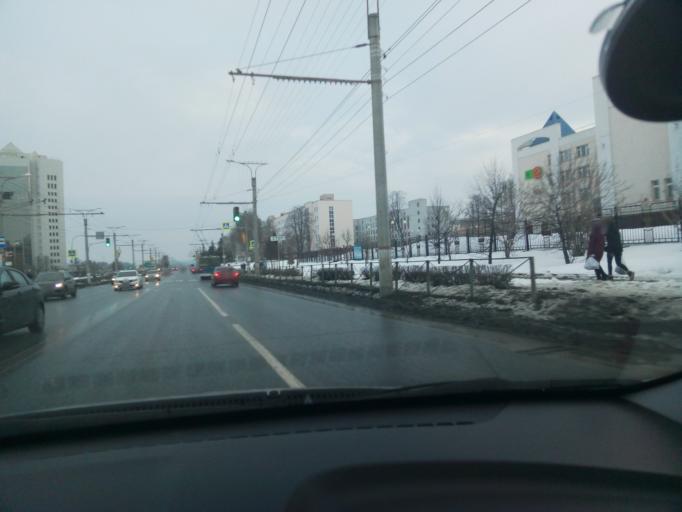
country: RU
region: Chuvashia
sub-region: Cheboksarskiy Rayon
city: Cheboksary
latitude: 56.1371
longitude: 47.2427
